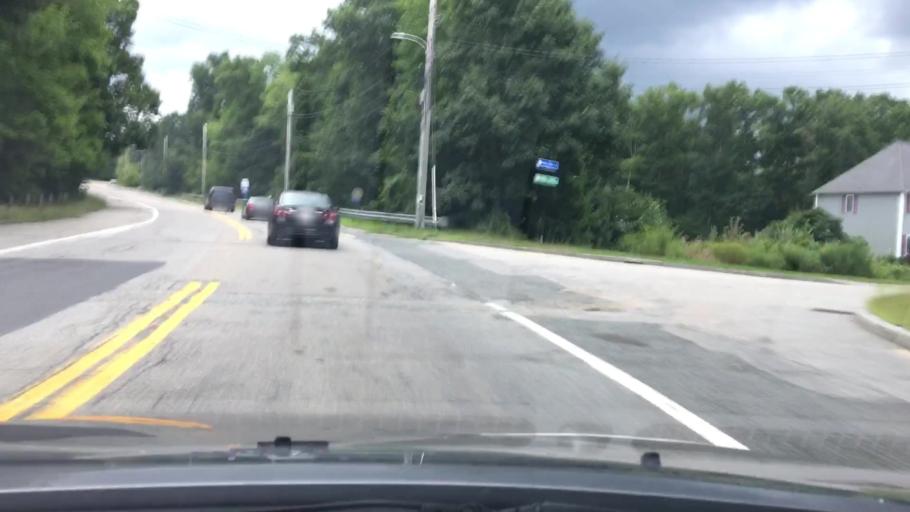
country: US
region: Rhode Island
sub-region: Providence County
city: Cumberland
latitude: 41.9713
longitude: -71.3811
